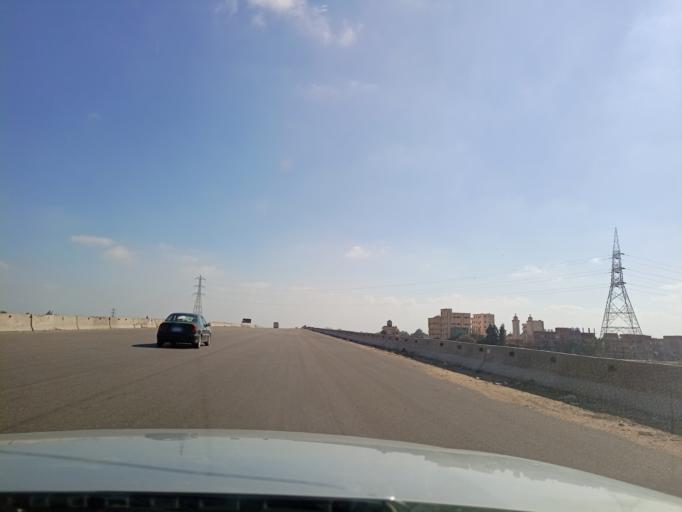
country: EG
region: Eastern Province
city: Mashtul as Suq
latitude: 30.4608
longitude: 31.3300
